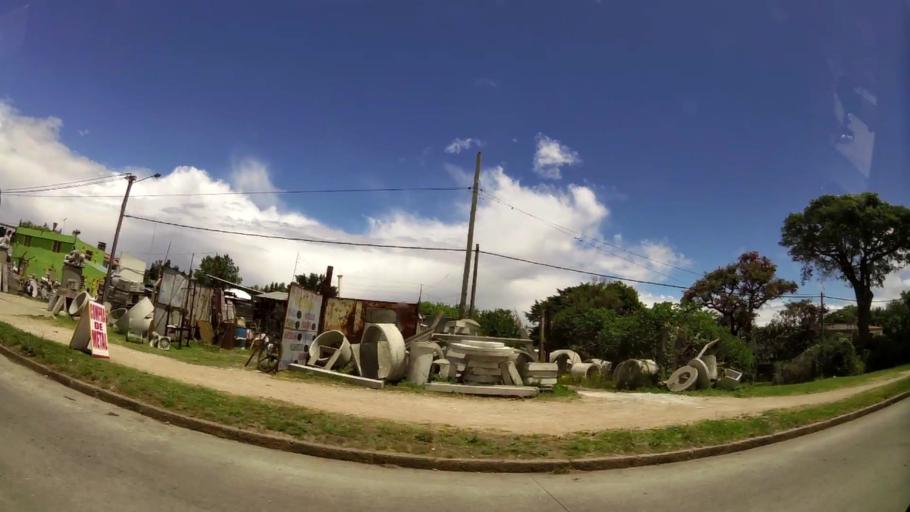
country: UY
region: Montevideo
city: Montevideo
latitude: -34.8346
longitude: -56.1883
